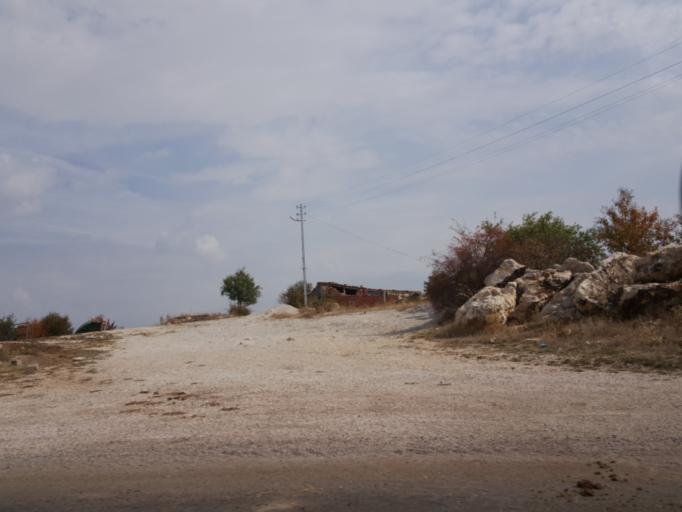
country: TR
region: Tokat
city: Zile
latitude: 40.3762
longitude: 35.8718
